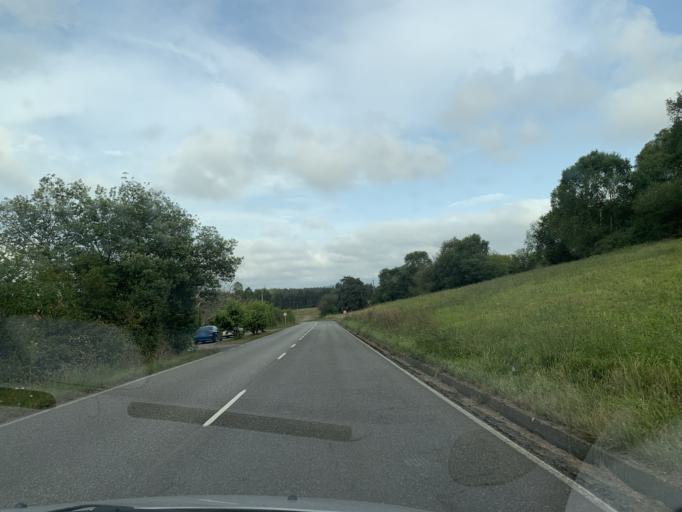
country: ES
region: Asturias
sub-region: Province of Asturias
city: Villaviciosa
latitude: 43.5171
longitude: -5.4324
